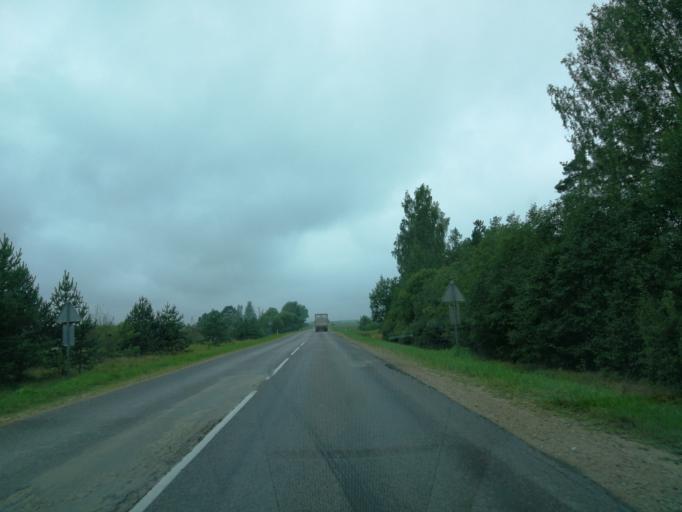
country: LV
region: Livani
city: Livani
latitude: 56.3498
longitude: 26.2643
